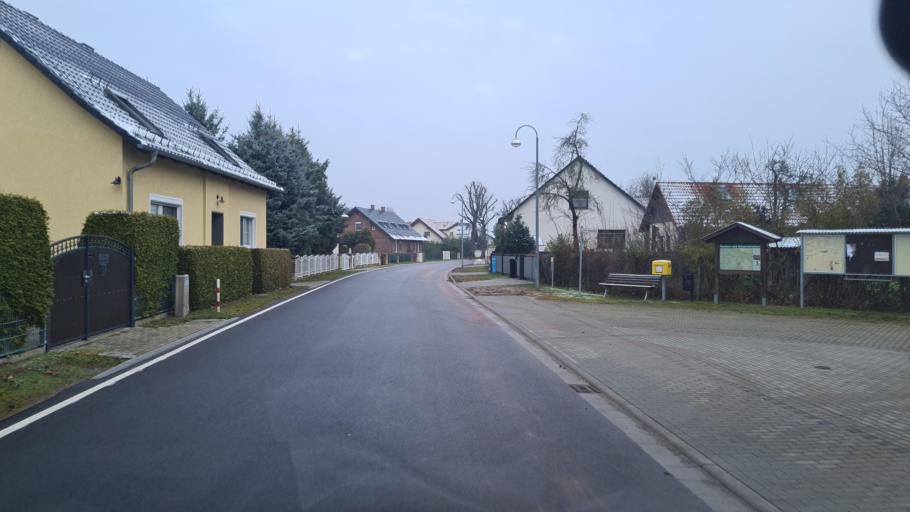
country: DE
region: Brandenburg
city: Storkow
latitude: 52.2885
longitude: 13.8810
